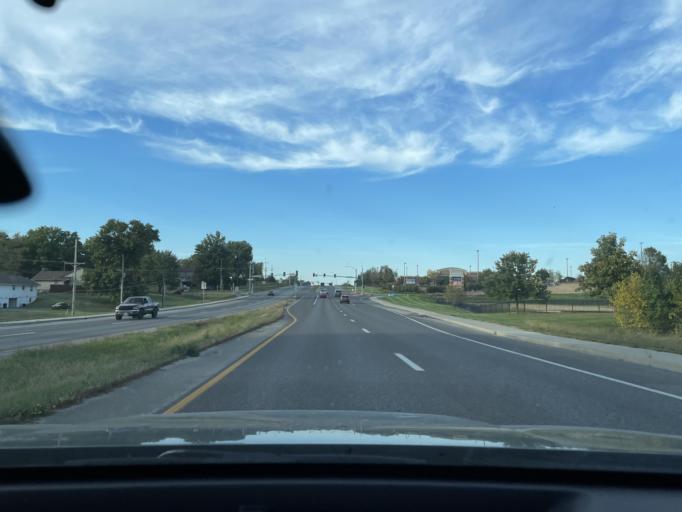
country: US
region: Missouri
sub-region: Andrew County
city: Country Club Village
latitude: 39.8095
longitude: -94.8151
